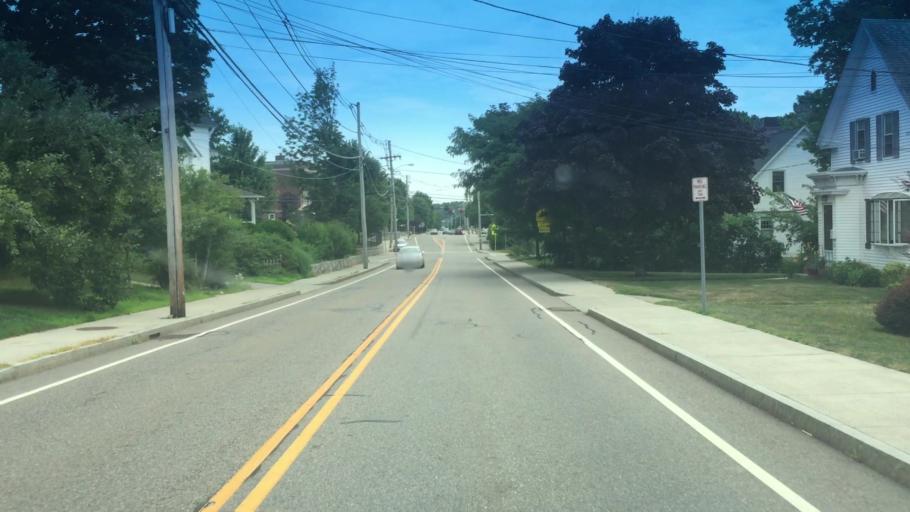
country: US
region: Massachusetts
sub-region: Norfolk County
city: Franklin
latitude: 42.0857
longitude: -71.4026
